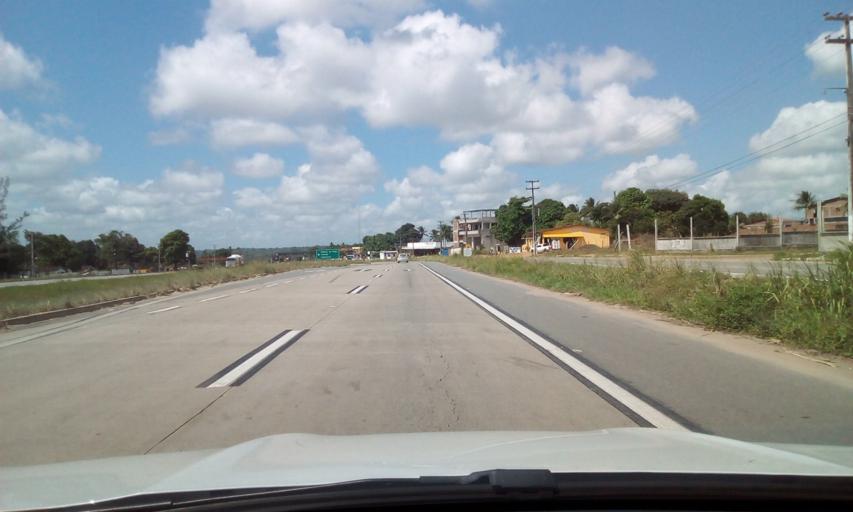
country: BR
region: Paraiba
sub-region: Alhandra
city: Alhandra
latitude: -7.3543
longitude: -34.9494
